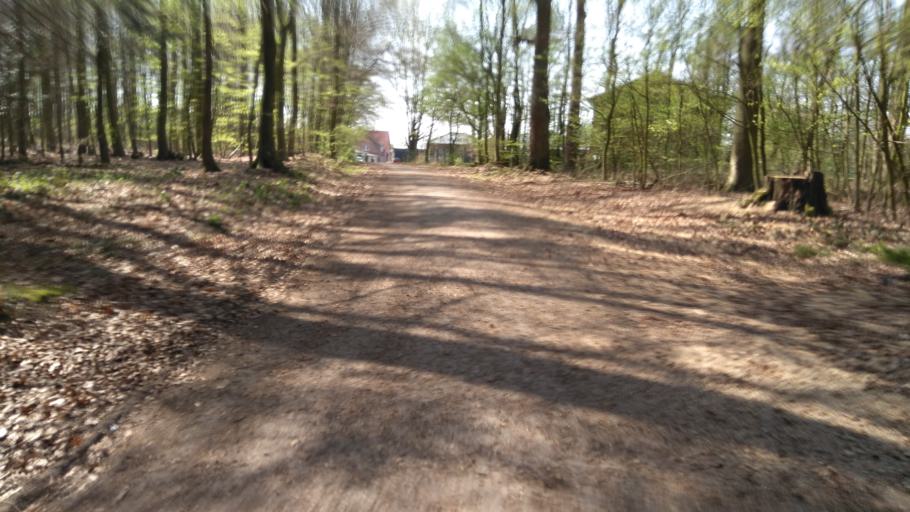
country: DE
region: Lower Saxony
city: Nottensdorf
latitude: 53.4782
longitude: 9.6227
